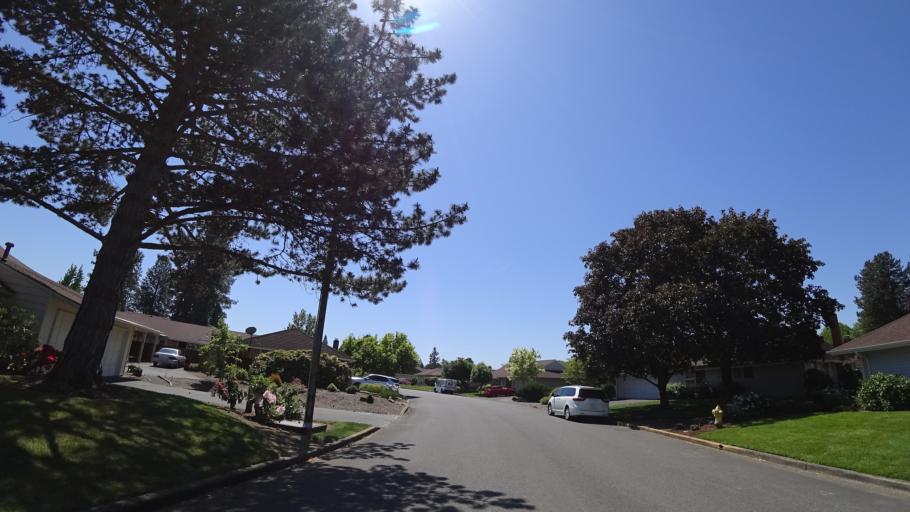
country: US
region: Oregon
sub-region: Washington County
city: Beaverton
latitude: 45.4838
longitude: -122.8243
